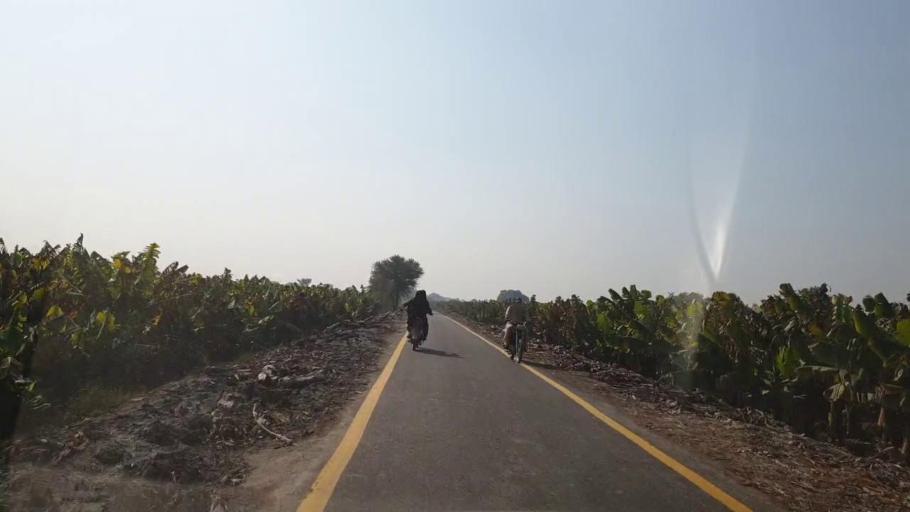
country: PK
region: Sindh
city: Matiari
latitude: 25.5354
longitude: 68.4931
